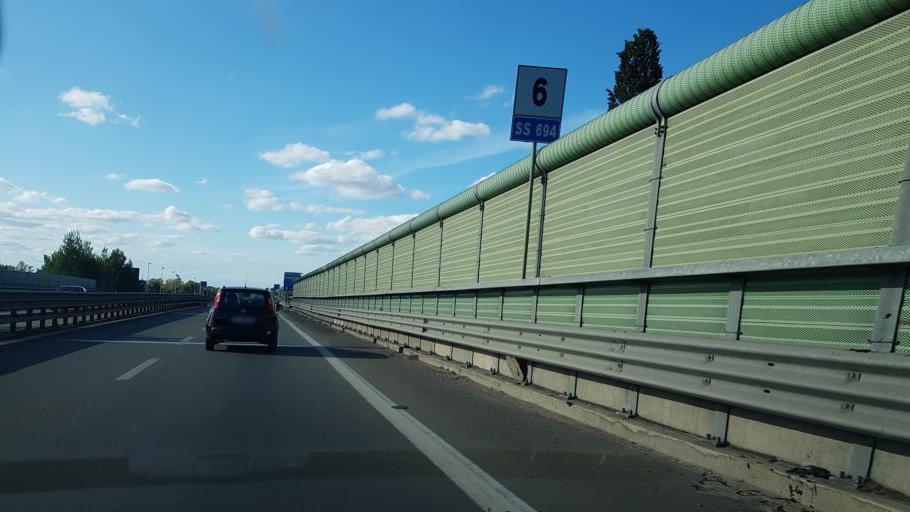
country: IT
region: Apulia
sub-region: Provincia di Lecce
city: Lequile
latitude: 40.3303
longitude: 18.1400
